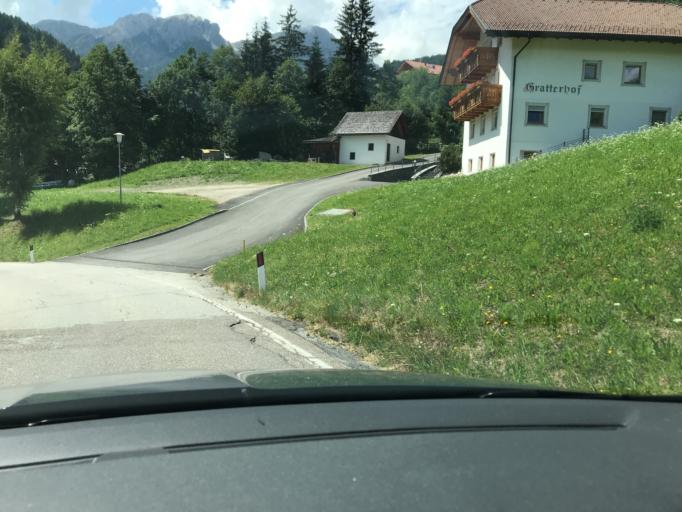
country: IT
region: Trentino-Alto Adige
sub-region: Bolzano
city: Valdaora di Mezzo
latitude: 46.7485
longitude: 12.0109
